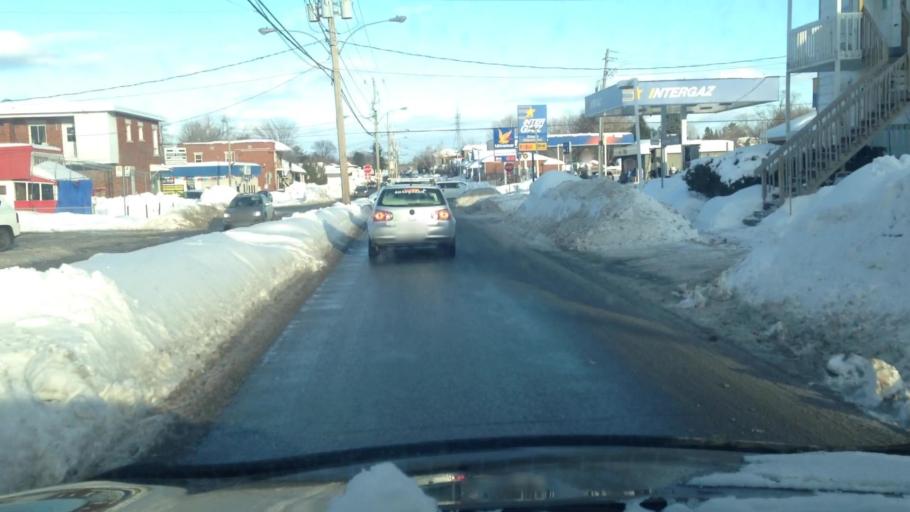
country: CA
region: Quebec
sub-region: Laurentides
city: Saint-Jerome
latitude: 45.7943
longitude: -74.0071
